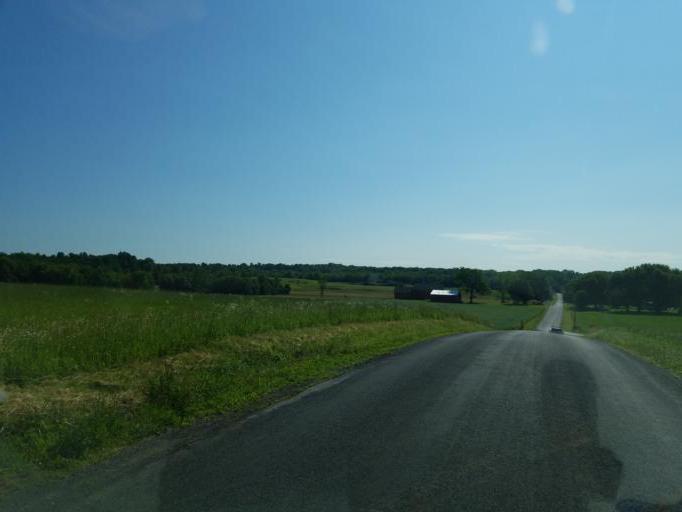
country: US
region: New York
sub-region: Wayne County
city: Clyde
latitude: 43.0549
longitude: -76.8859
